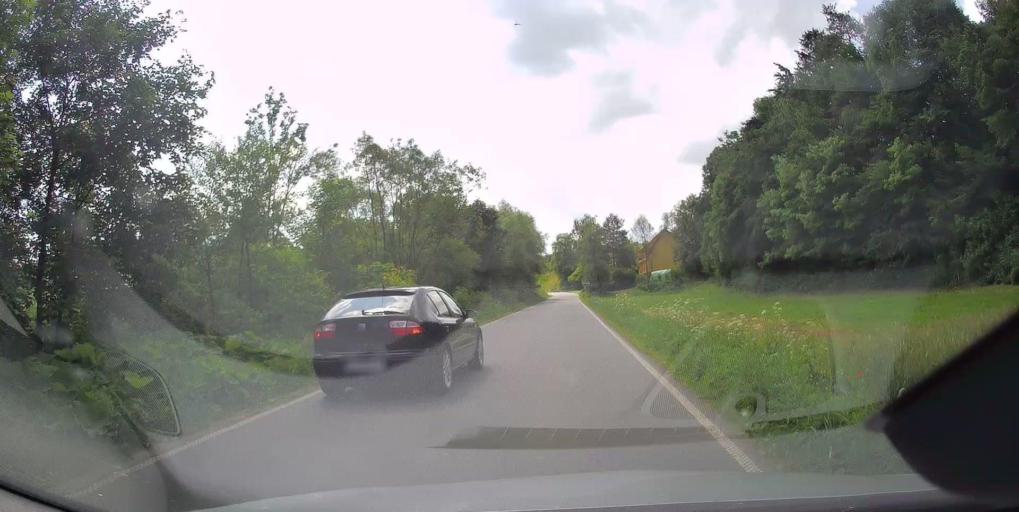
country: PL
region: Lesser Poland Voivodeship
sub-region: Powiat nowosadecki
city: Korzenna
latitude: 49.7384
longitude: 20.7707
